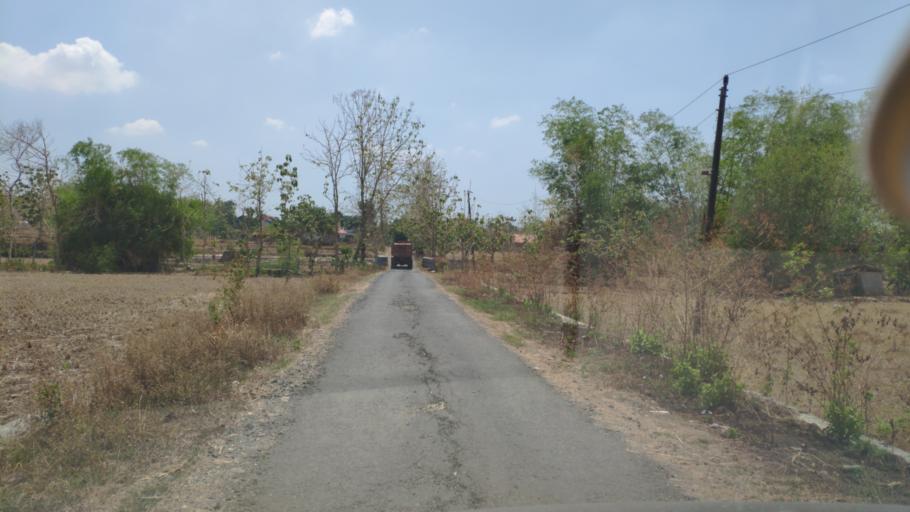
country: ID
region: Central Java
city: Karangjati
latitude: -6.9512
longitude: 111.4248
